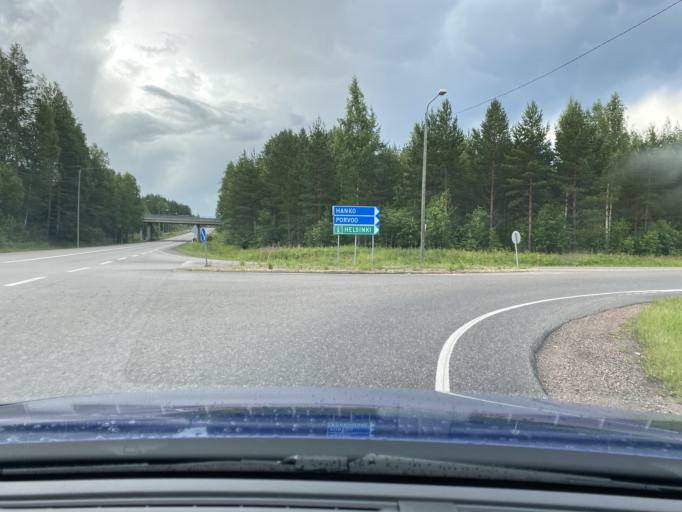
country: FI
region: Uusimaa
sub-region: Helsinki
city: Hyvinge
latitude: 60.5645
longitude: 24.8133
